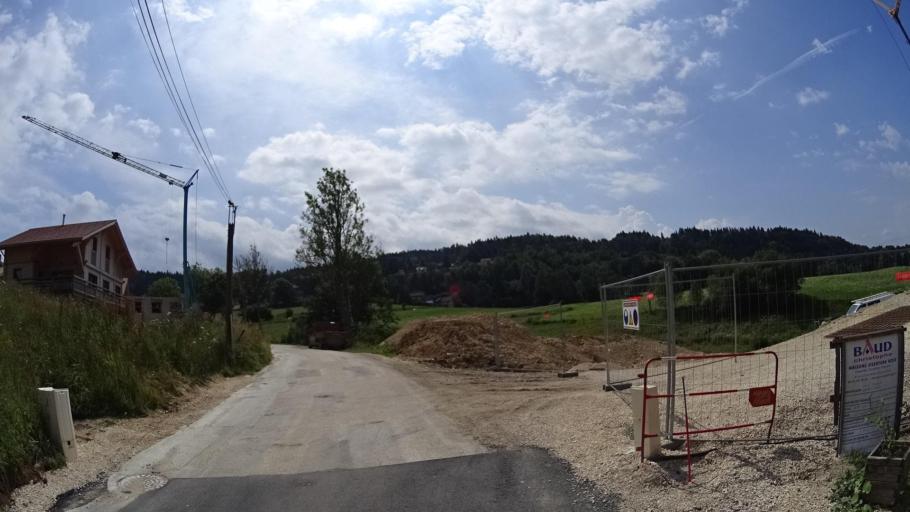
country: FR
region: Franche-Comte
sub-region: Departement du Doubs
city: Les Fourgs
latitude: 46.8365
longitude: 6.3426
